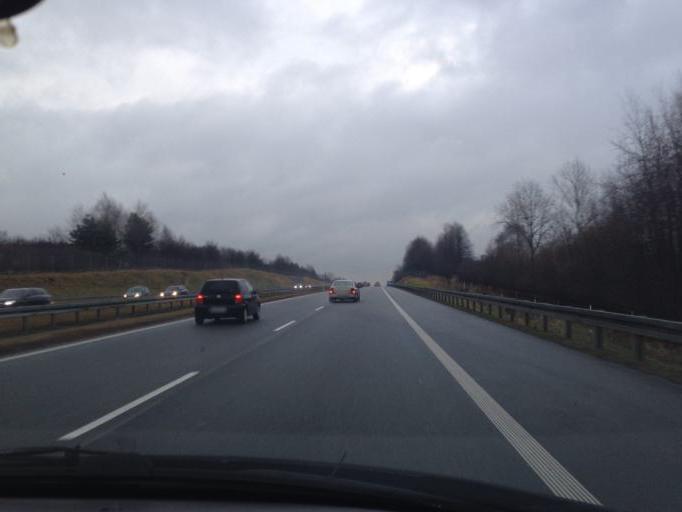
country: PL
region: Lesser Poland Voivodeship
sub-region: Powiat chrzanowski
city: Balin
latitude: 50.1532
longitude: 19.3722
